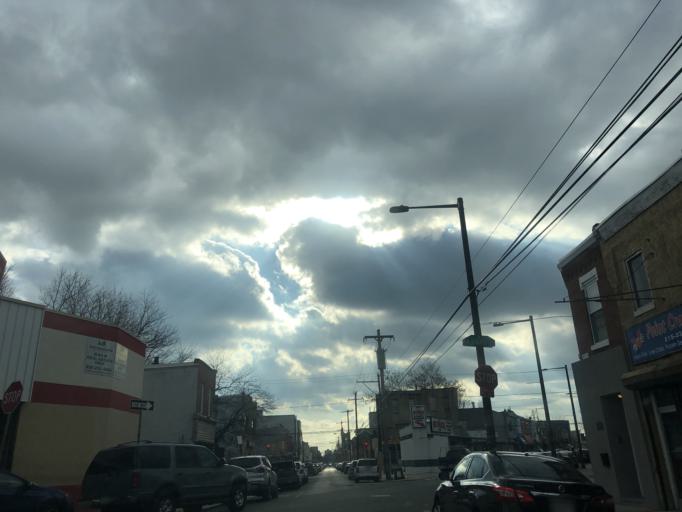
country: US
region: Pennsylvania
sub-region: Philadelphia County
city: Philadelphia
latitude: 39.9351
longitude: -75.1792
